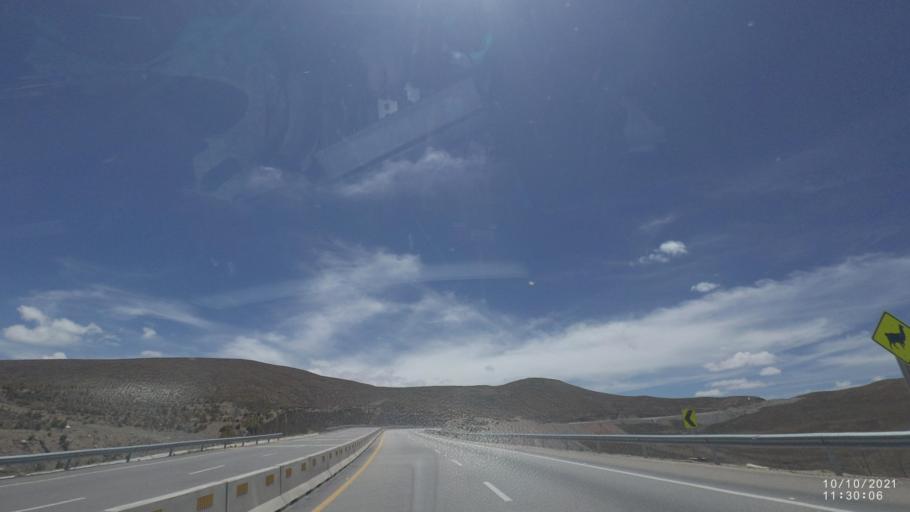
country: BO
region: La Paz
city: Colquiri
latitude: -17.6371
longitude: -66.8857
